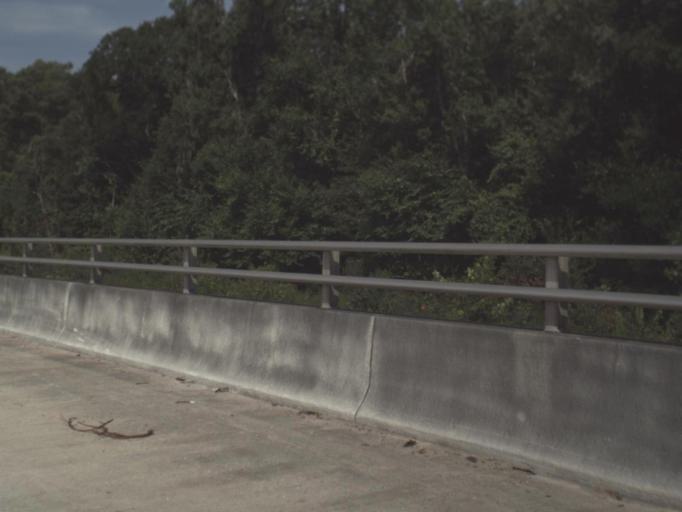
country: US
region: Florida
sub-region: Putnam County
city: East Palatka
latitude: 29.7235
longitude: -81.4851
